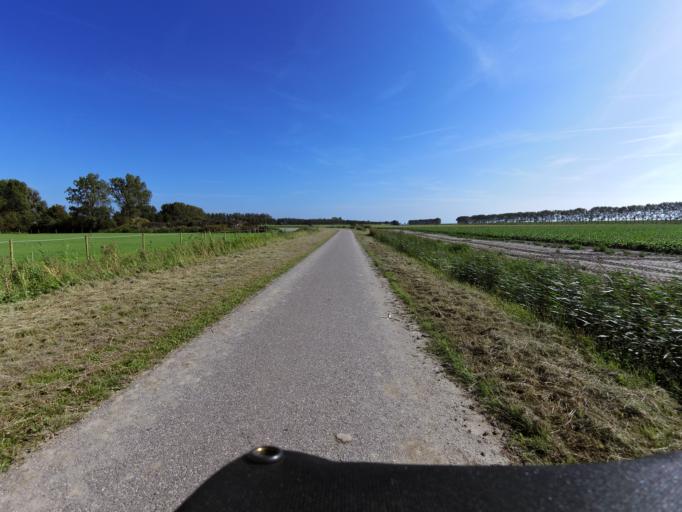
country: NL
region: South Holland
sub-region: Gemeente Goeree-Overflakkee
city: Dirksland
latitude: 51.7492
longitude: 4.0616
